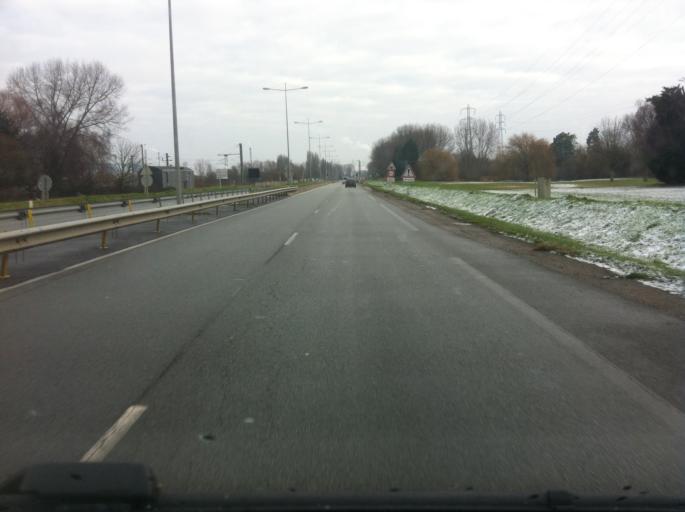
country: FR
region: Haute-Normandie
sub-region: Departement de la Seine-Maritime
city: Harfleur
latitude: 49.4877
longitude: 0.1978
